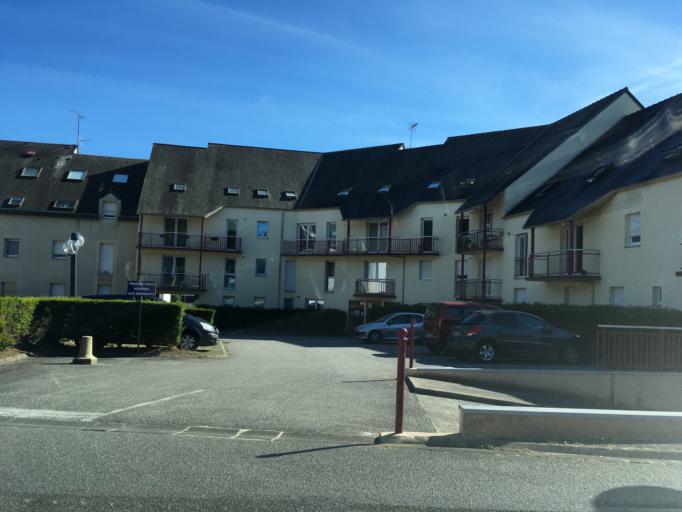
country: FR
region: Brittany
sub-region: Departement du Finistere
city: Quimper
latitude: 47.9863
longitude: -4.0872
